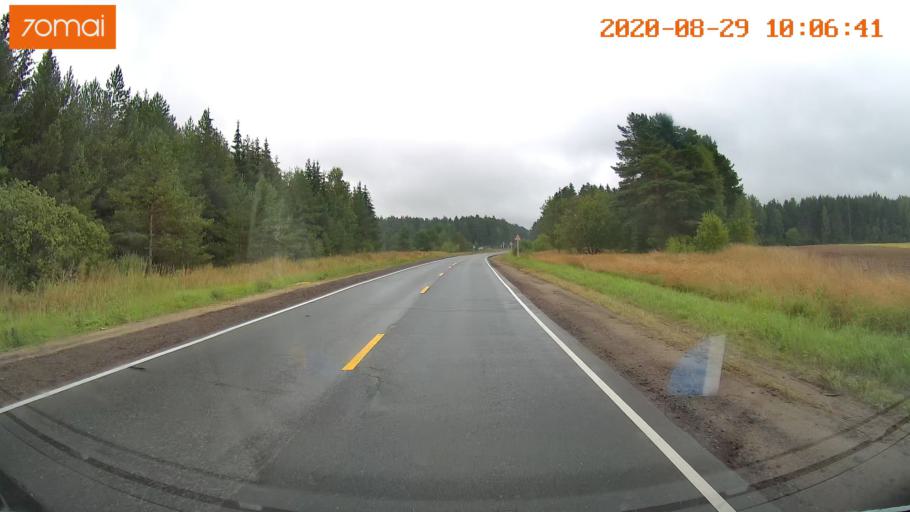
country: RU
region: Ivanovo
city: Kuznechikha
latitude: 57.3871
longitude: 42.5513
